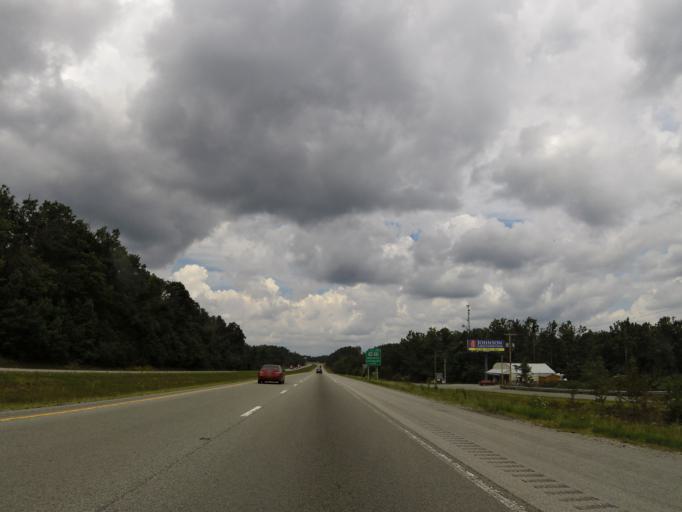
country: US
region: Tennessee
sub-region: Putnam County
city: Monterey
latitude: 36.1243
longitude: -85.2542
